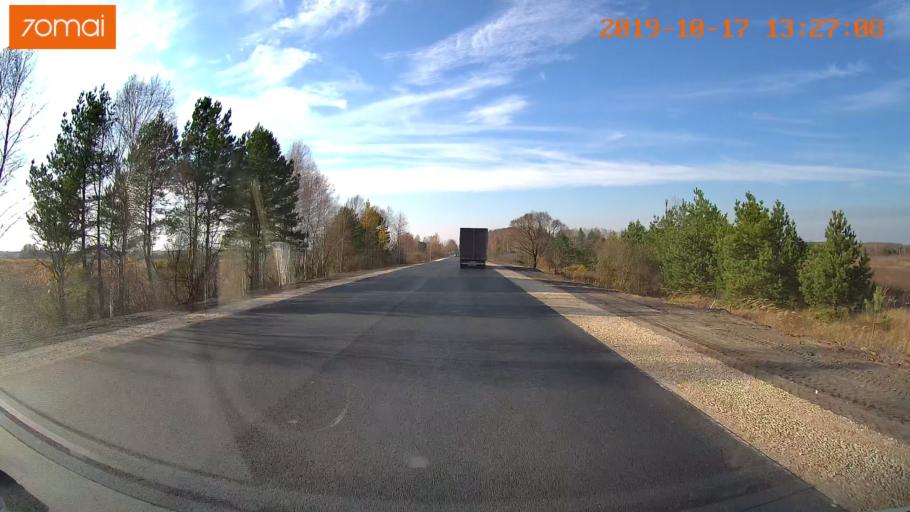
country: RU
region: Rjazan
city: Gus'-Zheleznyy
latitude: 55.1127
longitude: 40.9024
